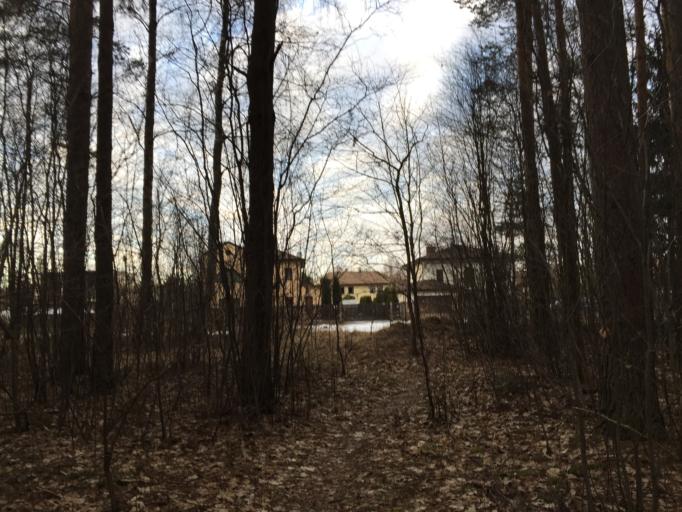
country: LV
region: Babite
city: Pinki
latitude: 56.9180
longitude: 23.8678
